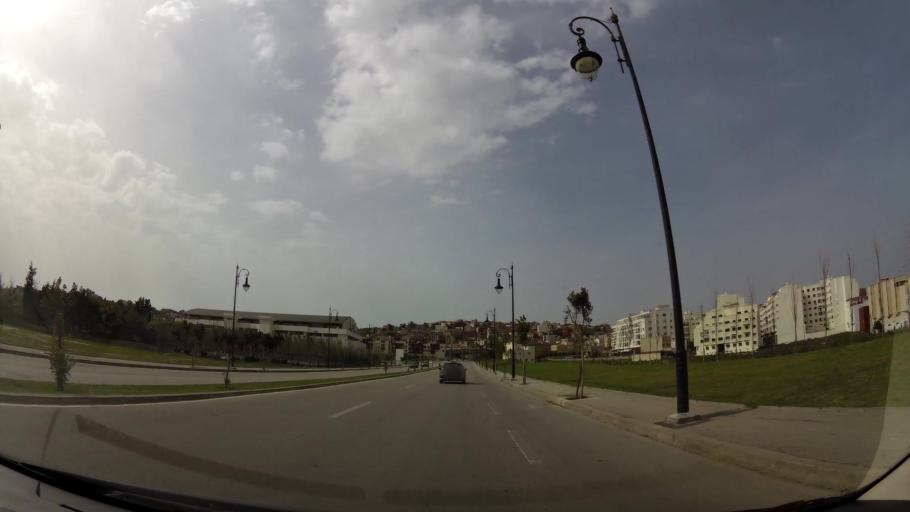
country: MA
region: Tanger-Tetouan
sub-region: Tanger-Assilah
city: Boukhalef
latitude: 35.7445
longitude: -5.8592
